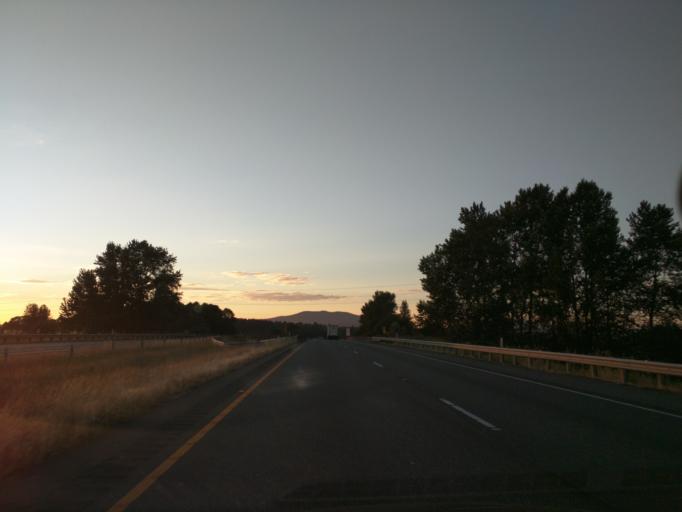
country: US
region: Washington
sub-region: Skagit County
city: Burlington
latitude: 48.5138
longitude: -122.3428
